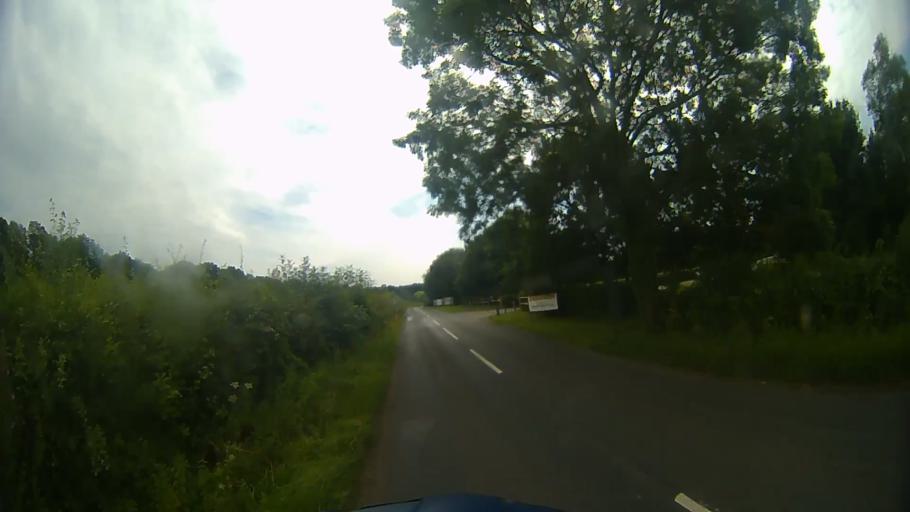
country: GB
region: England
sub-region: Hampshire
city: Kingsley
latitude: 51.1630
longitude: -0.8544
